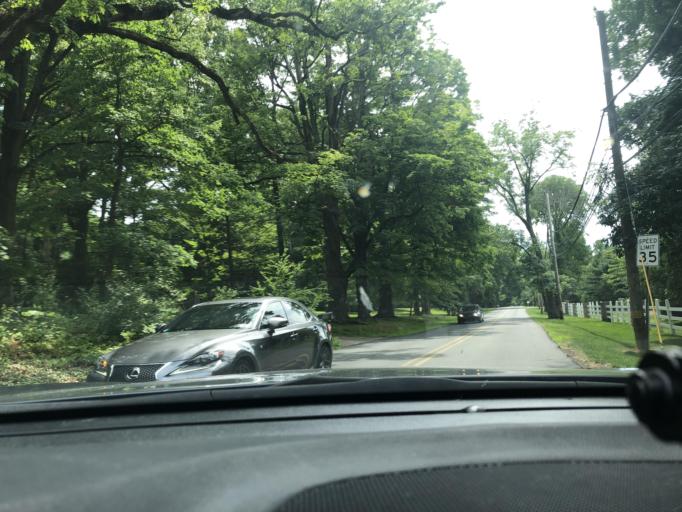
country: US
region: Pennsylvania
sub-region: Montgomery County
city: Ambler
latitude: 40.1552
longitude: -75.2405
